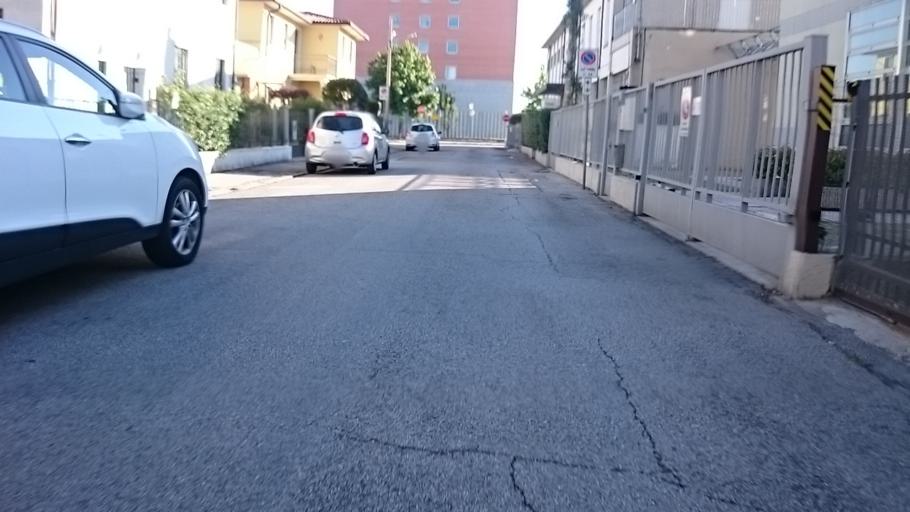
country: IT
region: Veneto
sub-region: Provincia di Padova
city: Padova
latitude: 45.4132
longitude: 11.8943
